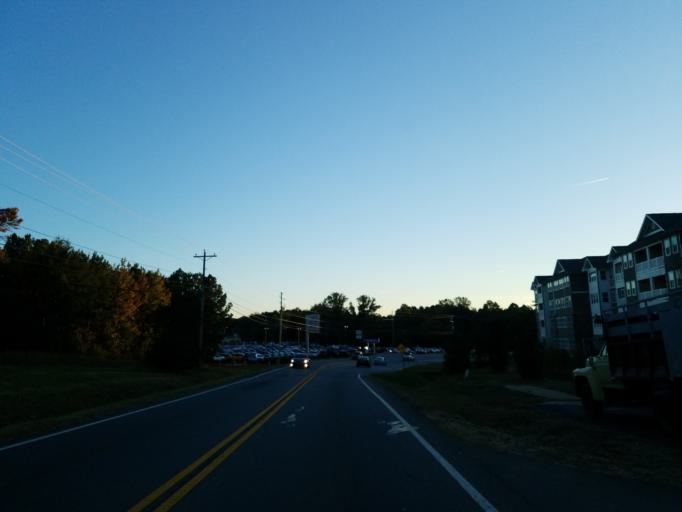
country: US
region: Georgia
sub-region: Forsyth County
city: Cumming
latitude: 34.1823
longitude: -84.1471
